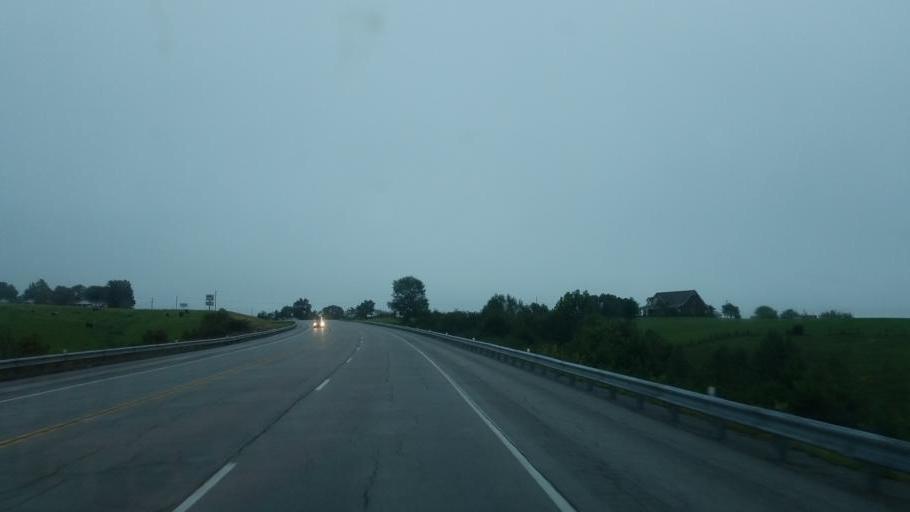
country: US
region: Kentucky
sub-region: Fleming County
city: Flemingsburg
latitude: 38.3956
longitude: -83.7133
